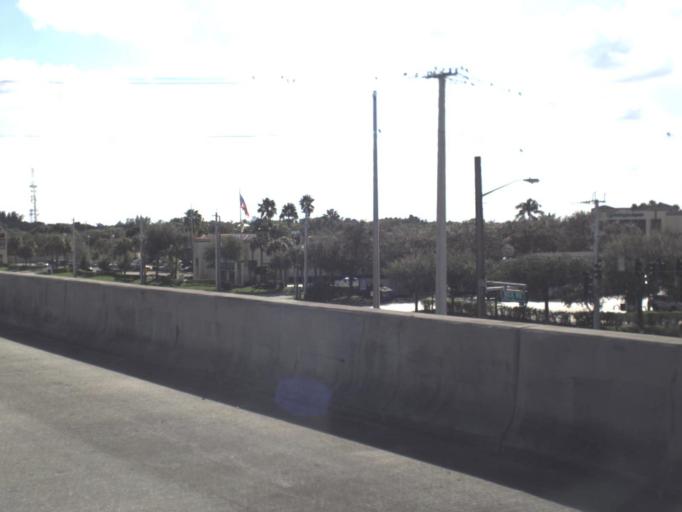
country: US
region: Florida
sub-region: Palm Beach County
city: Boca Del Mar
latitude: 26.3681
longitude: -80.1710
